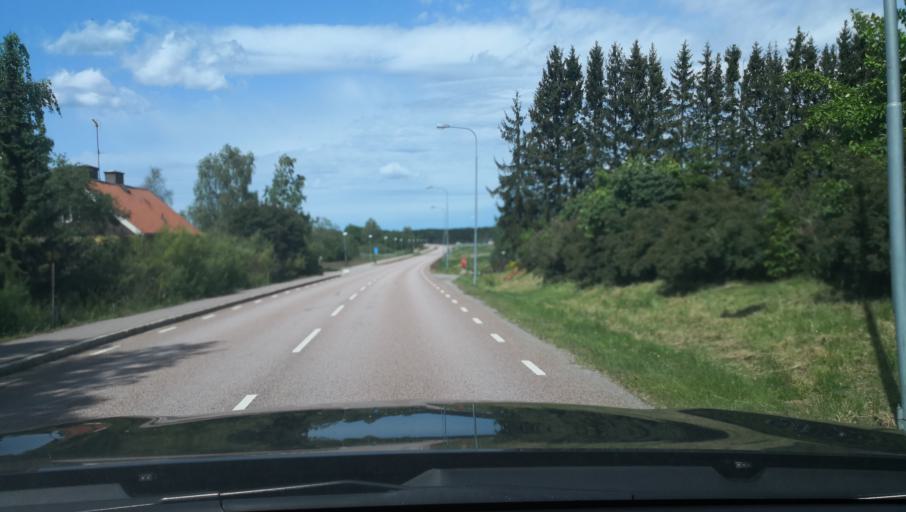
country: SE
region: Vaestmanland
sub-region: Surahammars Kommun
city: Ramnas
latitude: 59.8718
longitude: 16.0852
